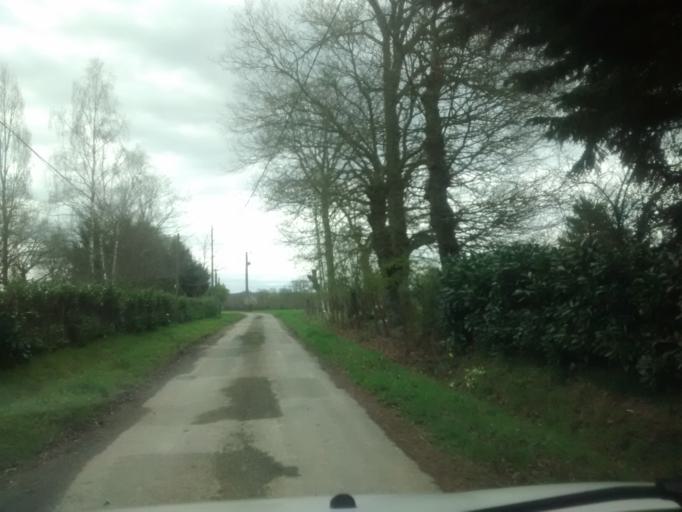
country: FR
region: Brittany
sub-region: Departement d'Ille-et-Vilaine
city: Chasne-sur-Illet
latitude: 48.2268
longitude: -1.5664
